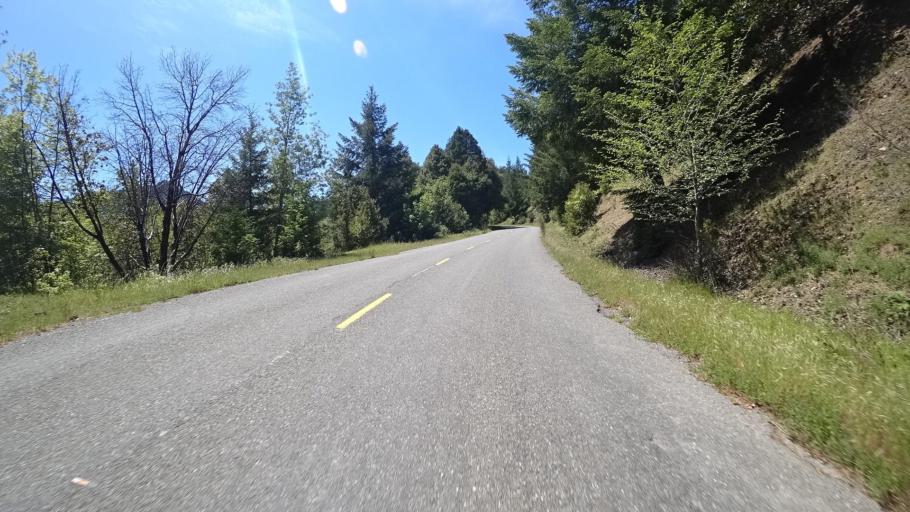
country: US
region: California
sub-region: Humboldt County
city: Rio Dell
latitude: 40.3317
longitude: -124.0289
